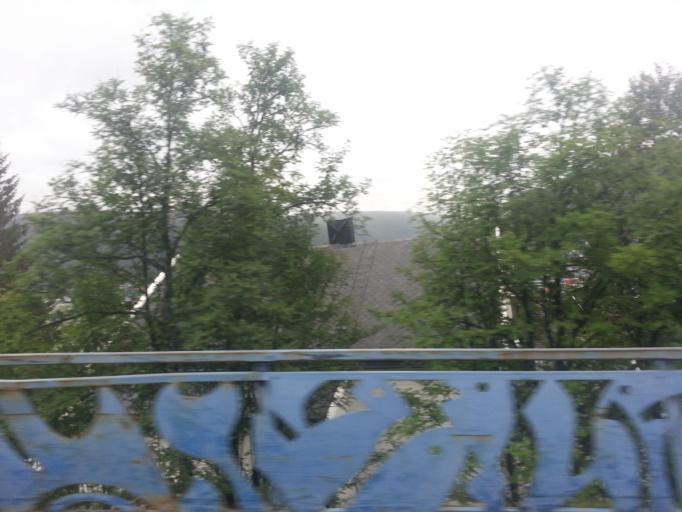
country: NO
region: Troms
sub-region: Tromso
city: Tromso
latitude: 69.6531
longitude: 18.9509
